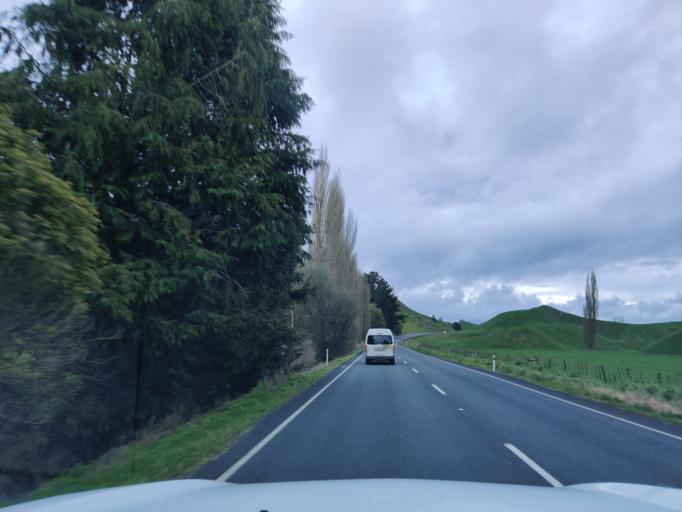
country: NZ
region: Waikato
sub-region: Otorohanga District
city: Otorohanga
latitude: -38.4716
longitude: 175.1723
